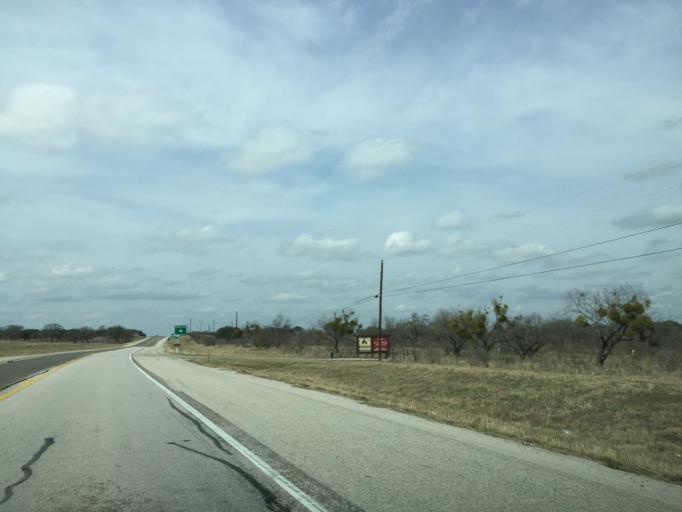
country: US
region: Texas
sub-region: Llano County
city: Horseshoe Bay
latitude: 30.5172
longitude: -98.4046
